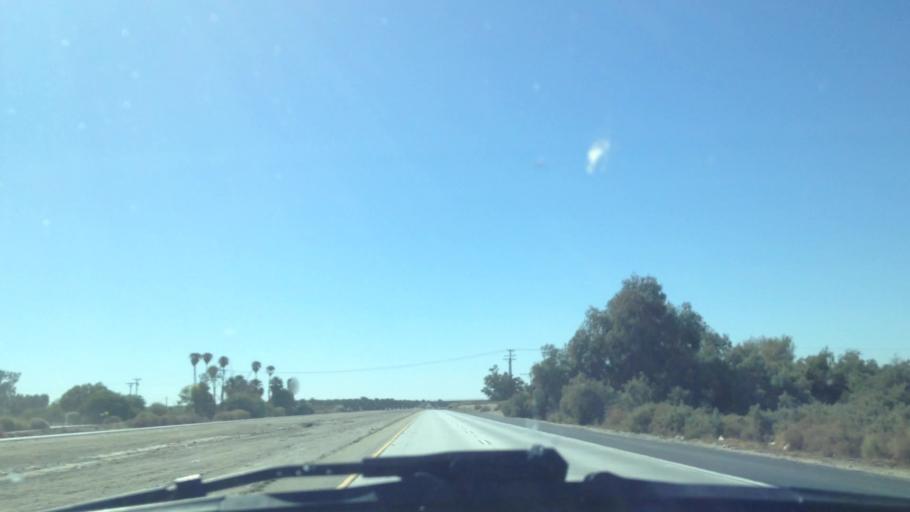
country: US
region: California
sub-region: Riverside County
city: Thermal
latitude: 33.6366
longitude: -116.1290
